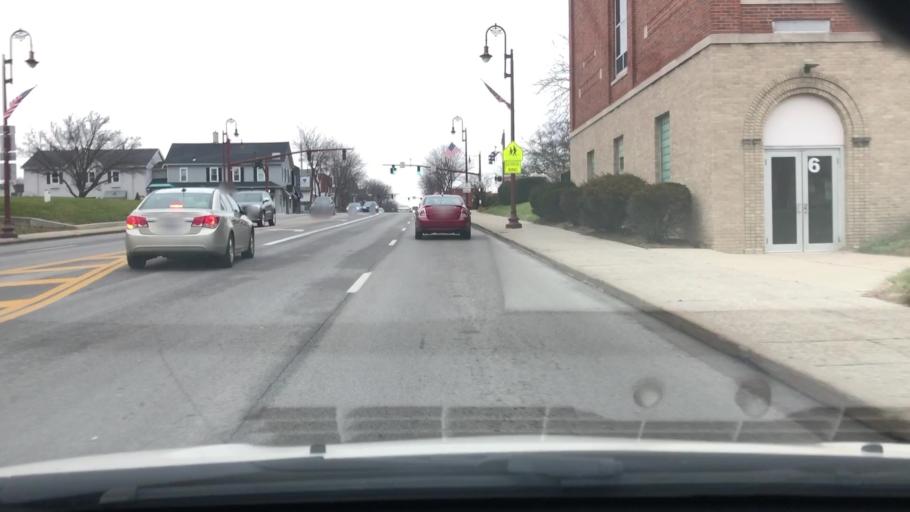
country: US
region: Ohio
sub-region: Lucas County
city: Maumee
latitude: 41.5603
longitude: -83.6524
